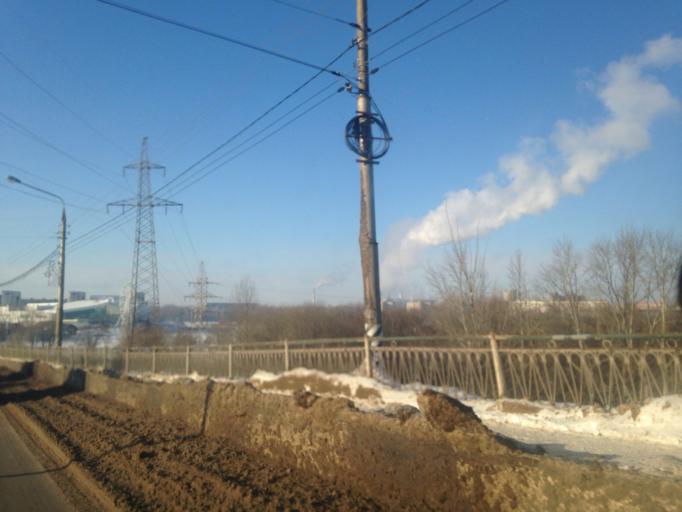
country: RU
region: Ulyanovsk
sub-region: Ulyanovskiy Rayon
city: Ulyanovsk
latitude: 54.3064
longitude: 48.3714
